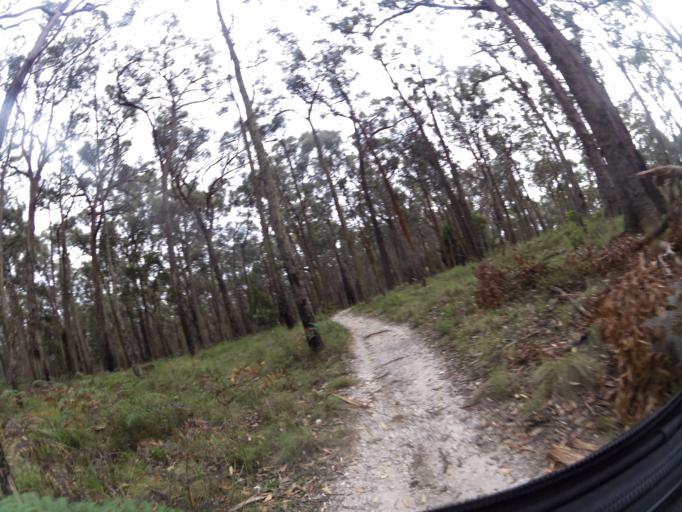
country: AU
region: Victoria
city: Brown Hill
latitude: -37.5230
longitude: 143.9070
